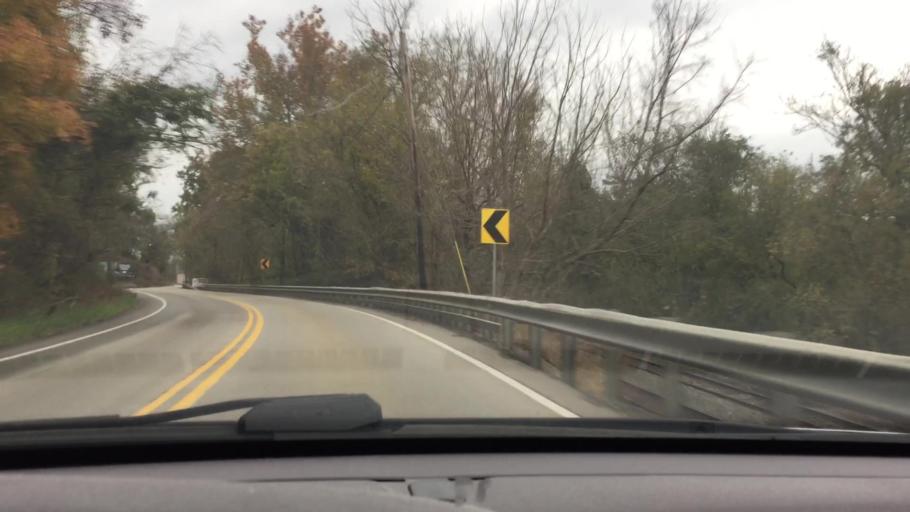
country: US
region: Pennsylvania
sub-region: Fayette County
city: Fairhope
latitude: 40.1061
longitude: -79.8478
